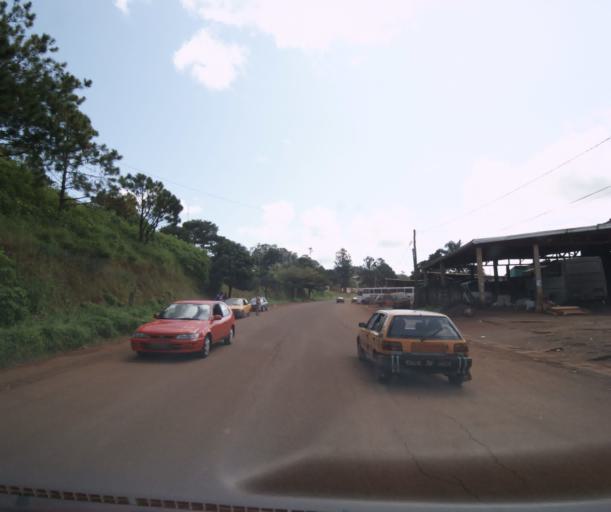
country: CM
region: West
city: Foumban
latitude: 5.7298
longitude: 10.8724
